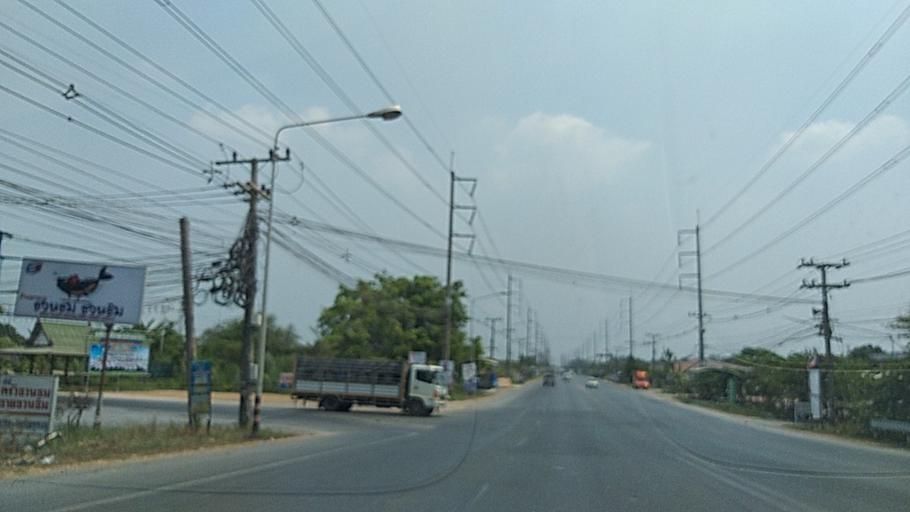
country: TH
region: Pathum Thani
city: Ban Lam Luk Ka
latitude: 13.9547
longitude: 100.8428
